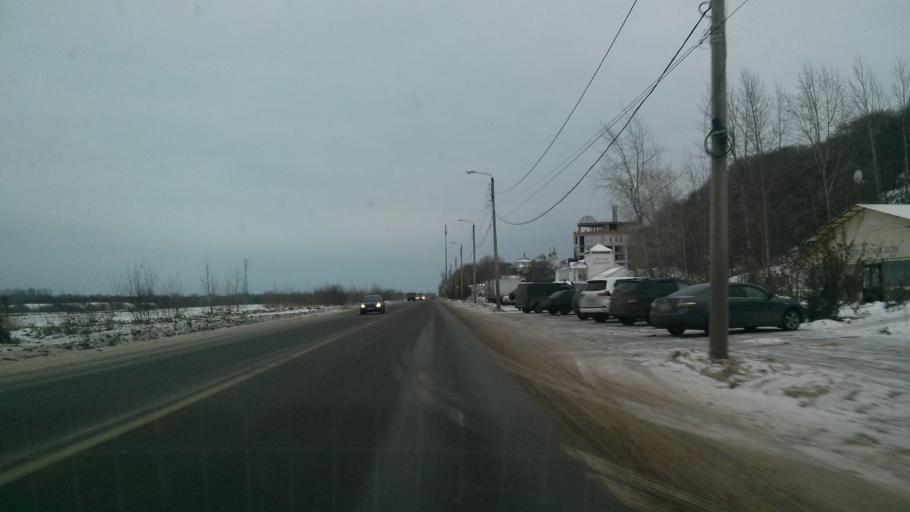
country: RU
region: Nizjnij Novgorod
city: Bor
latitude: 56.3225
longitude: 44.0612
